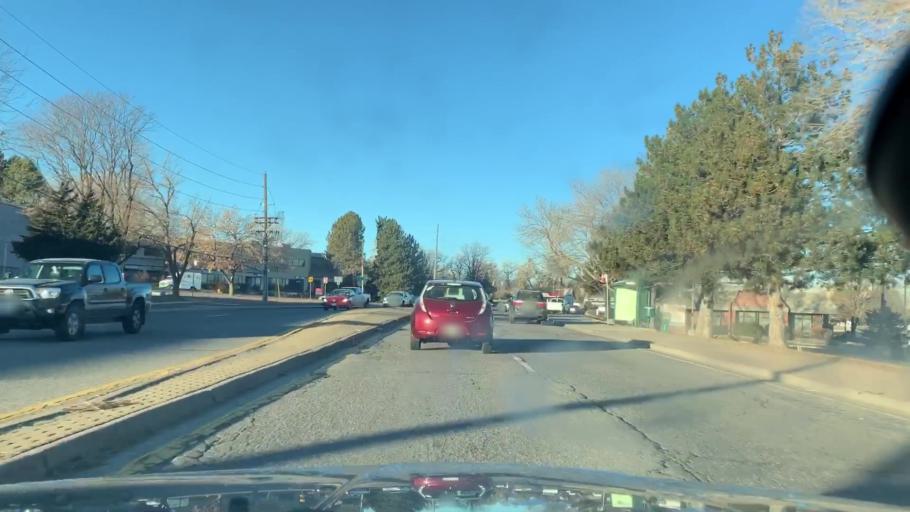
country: US
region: Colorado
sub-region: Arapahoe County
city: Glendale
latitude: 39.6750
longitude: -104.9002
